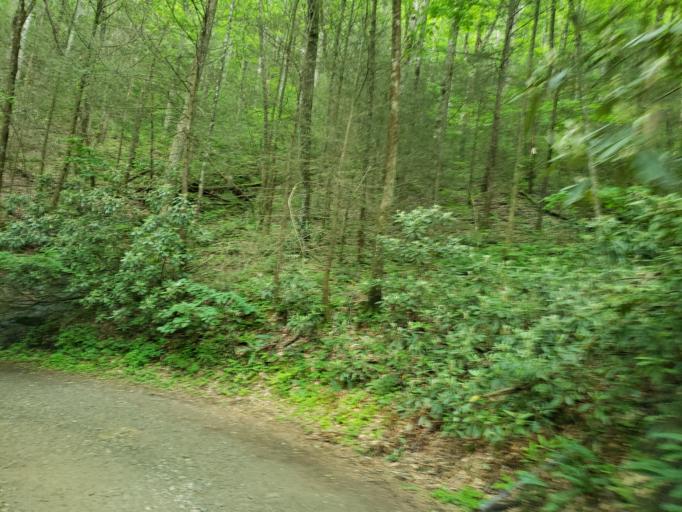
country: US
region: Georgia
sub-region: Fannin County
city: Blue Ridge
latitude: 34.8465
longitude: -84.4431
